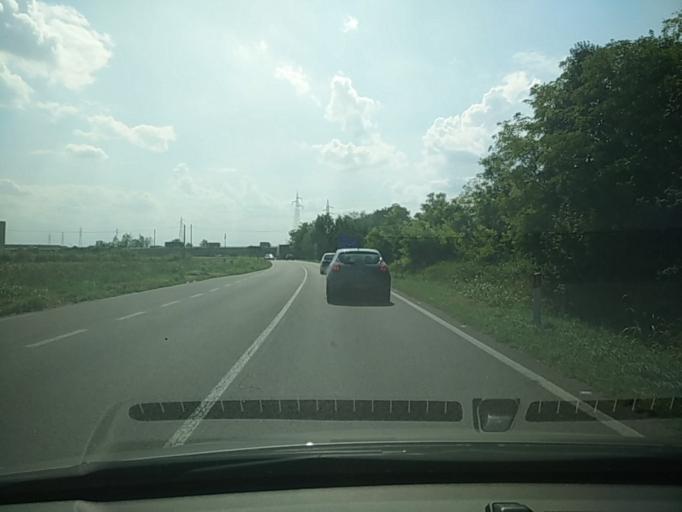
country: IT
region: Veneto
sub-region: Provincia di Treviso
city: Salvatronda
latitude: 45.6880
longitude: 11.9709
